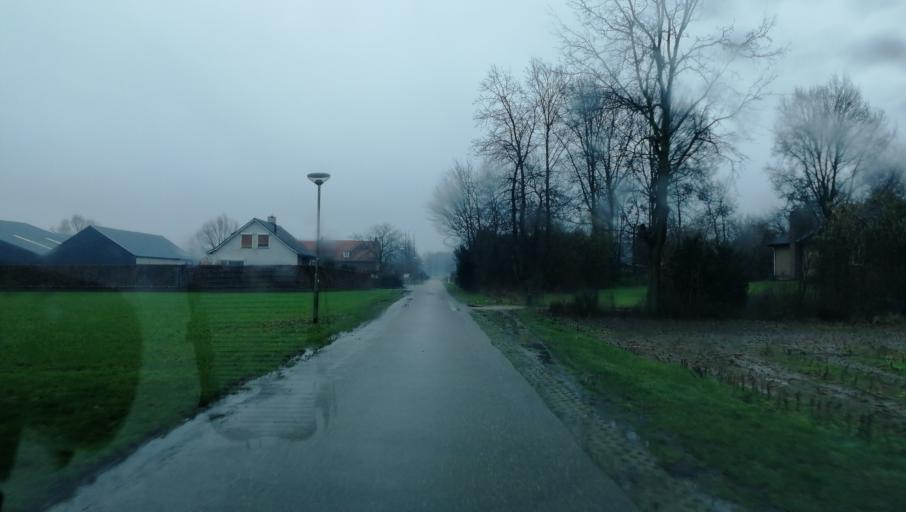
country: NL
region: Limburg
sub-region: Gemeente Venlo
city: Tegelen
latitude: 51.3592
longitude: 6.1147
